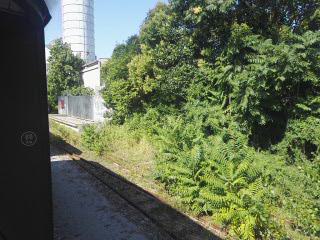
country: SI
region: Nova Gorica
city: Solkan
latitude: 45.9665
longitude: 13.6396
